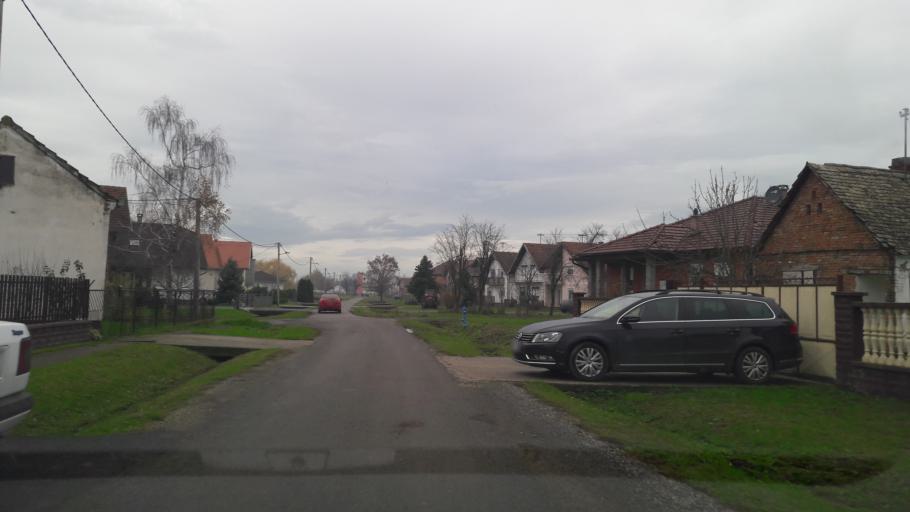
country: HR
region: Osjecko-Baranjska
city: Koska
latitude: 45.5420
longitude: 18.2902
